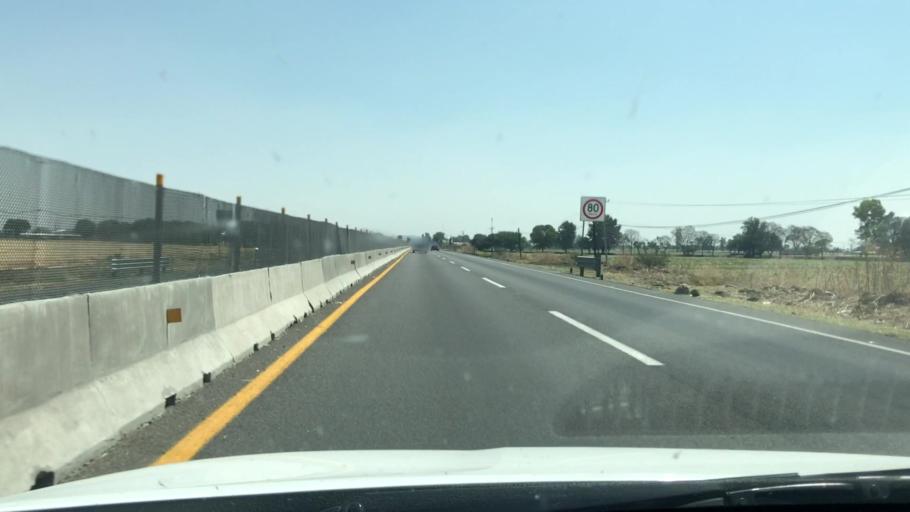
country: MX
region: Guanajuato
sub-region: Abasolo
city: San Bernardo Pena Blanca
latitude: 20.4822
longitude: -101.4946
